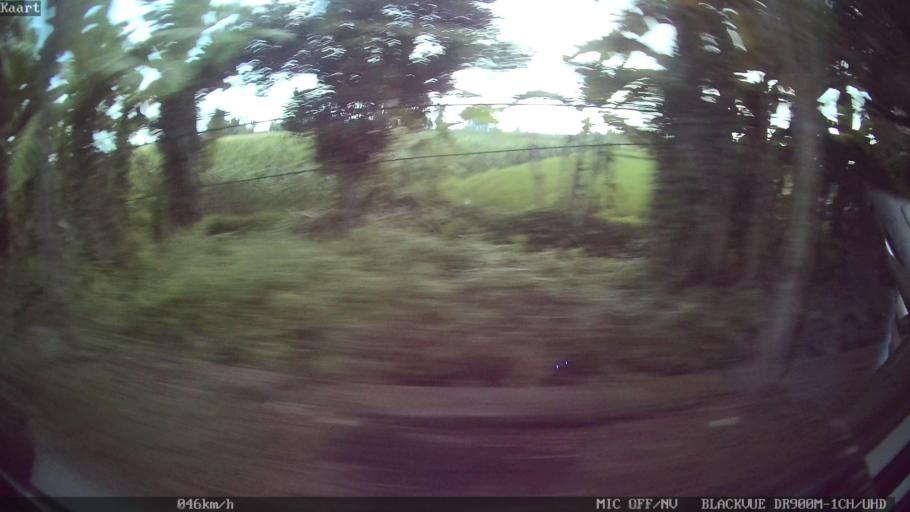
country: ID
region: Bali
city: Banjar Mambalkajanan
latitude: -8.5546
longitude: 115.2317
